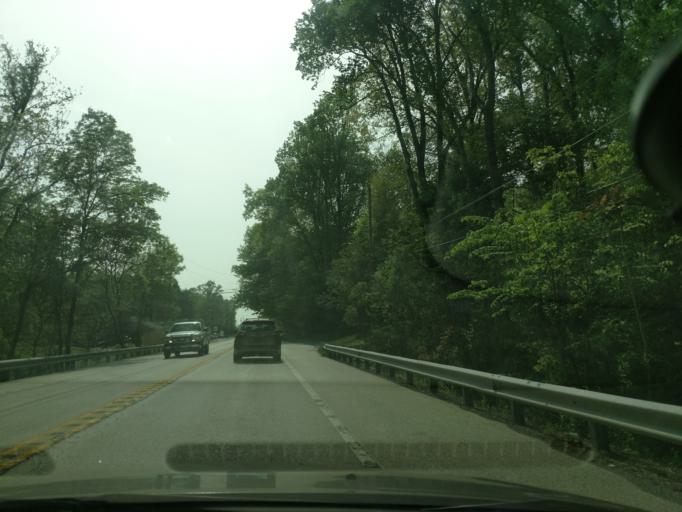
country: US
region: Pennsylvania
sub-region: Chester County
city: Elverson
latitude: 40.1624
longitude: -75.7837
